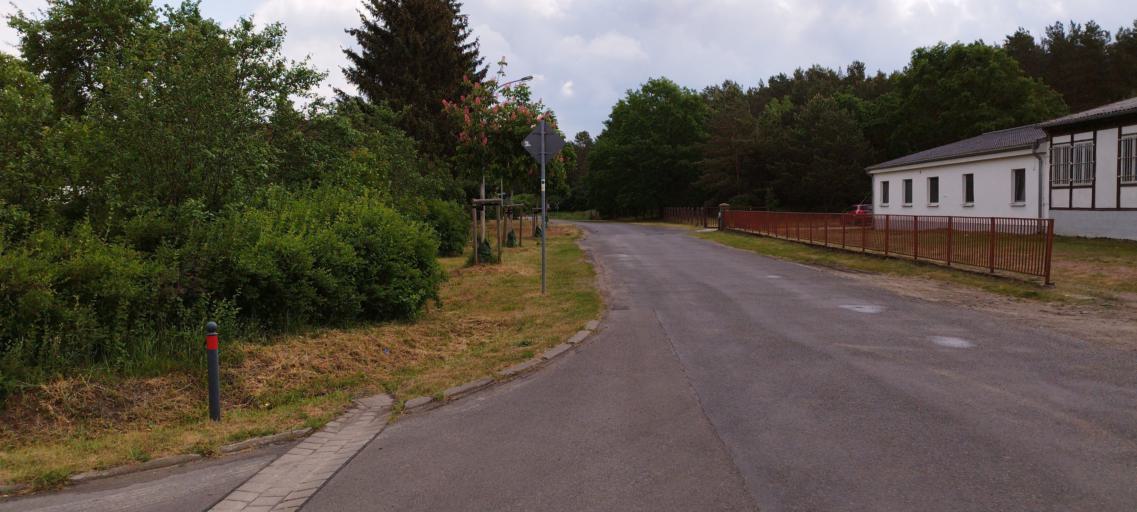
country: DE
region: Brandenburg
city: Furstenwalde
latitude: 52.3654
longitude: 14.0743
